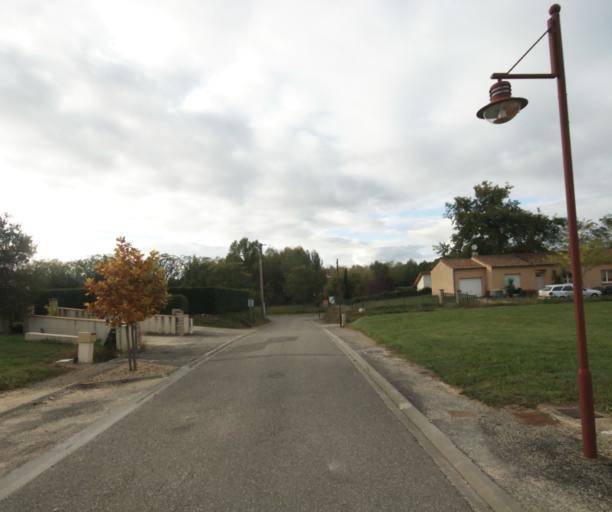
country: FR
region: Aquitaine
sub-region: Departement des Landes
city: Gabarret
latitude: 43.9508
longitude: 0.0896
